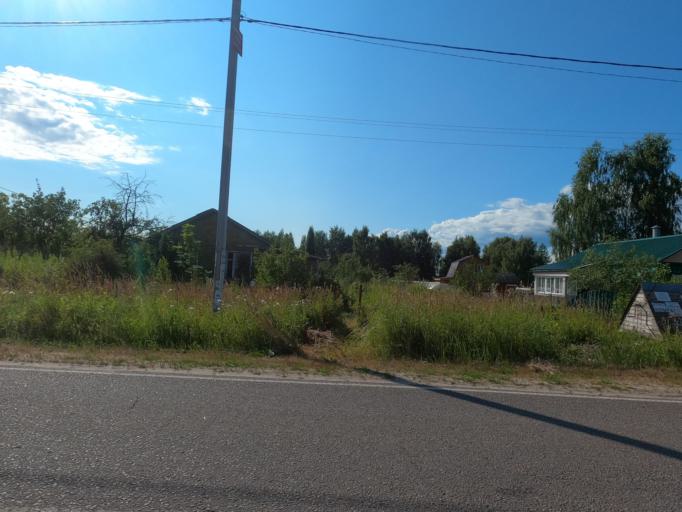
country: RU
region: Moskovskaya
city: Lopatinskiy
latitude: 55.3950
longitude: 38.7173
